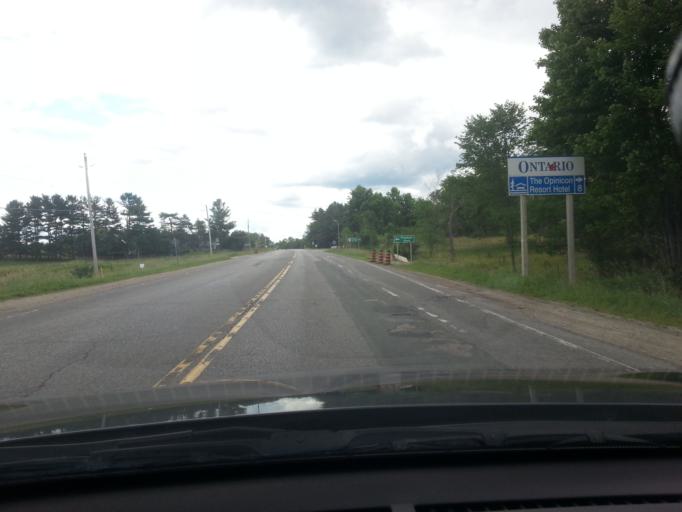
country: CA
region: Ontario
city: Perth
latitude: 44.6336
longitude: -76.2533
